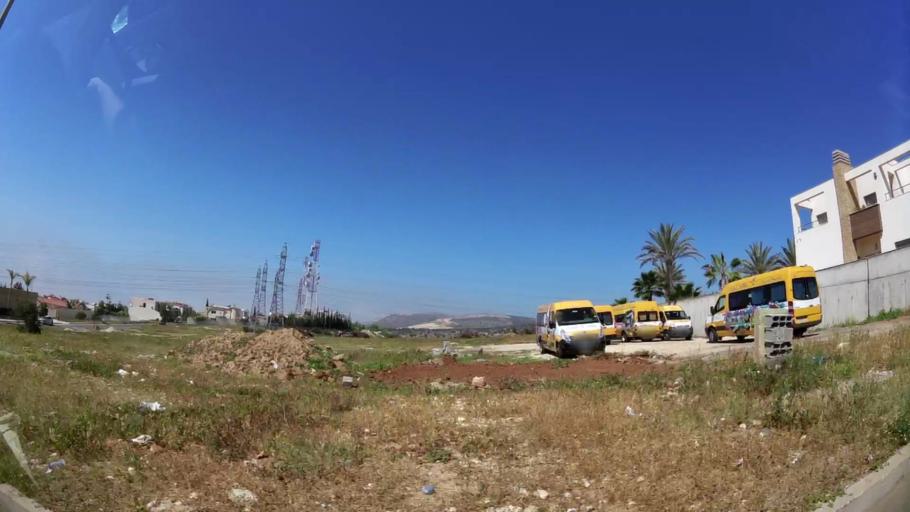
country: MA
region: Souss-Massa-Draa
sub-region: Agadir-Ida-ou-Tnan
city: Agadir
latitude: 30.4416
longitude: -9.5949
